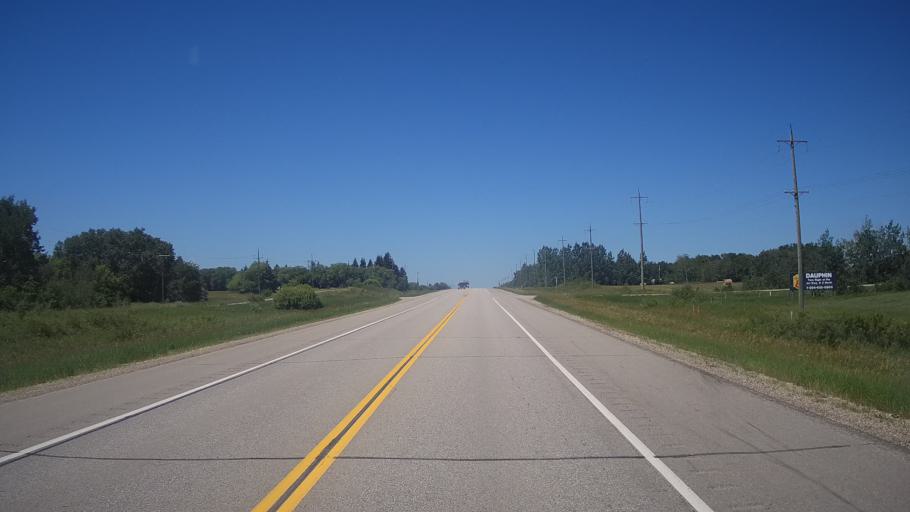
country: CA
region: Manitoba
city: Neepawa
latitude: 50.2254
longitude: -99.3624
